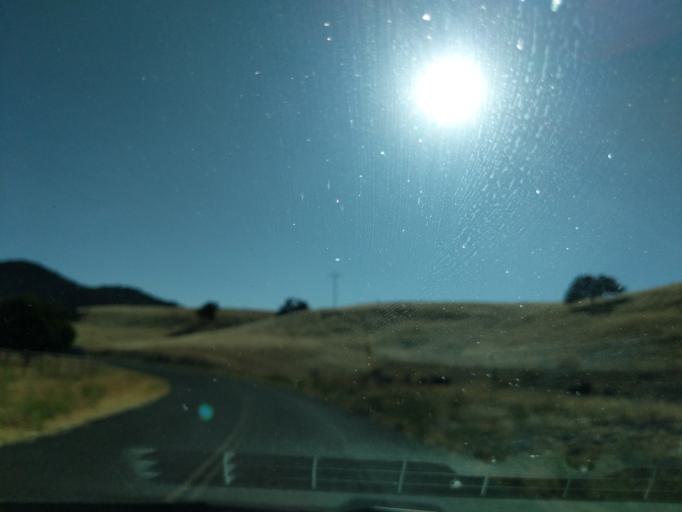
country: US
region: California
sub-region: Monterey County
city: King City
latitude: 36.1882
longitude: -120.8093
